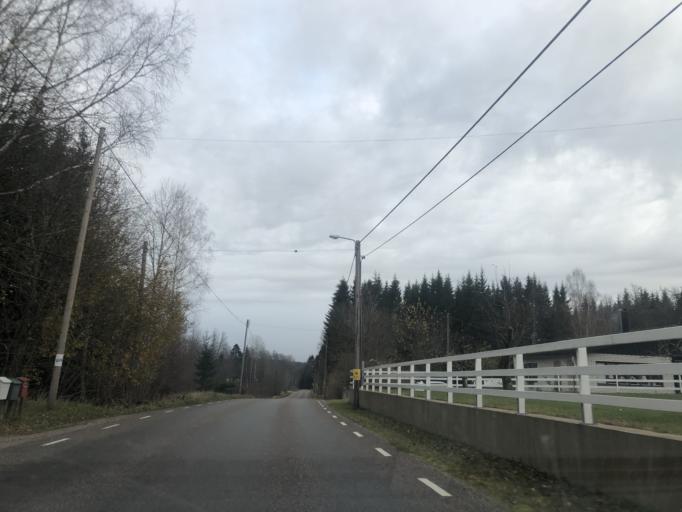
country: SE
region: Vaestra Goetaland
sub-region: Ulricehamns Kommun
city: Ulricehamn
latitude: 57.8006
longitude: 13.3461
